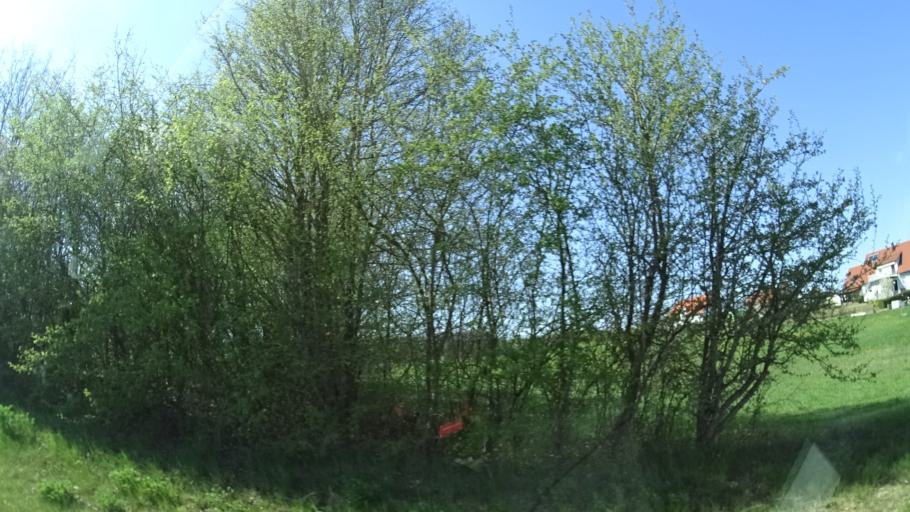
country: DE
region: Bavaria
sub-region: Upper Palatinate
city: Edelsfeld
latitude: 49.5455
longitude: 11.7247
